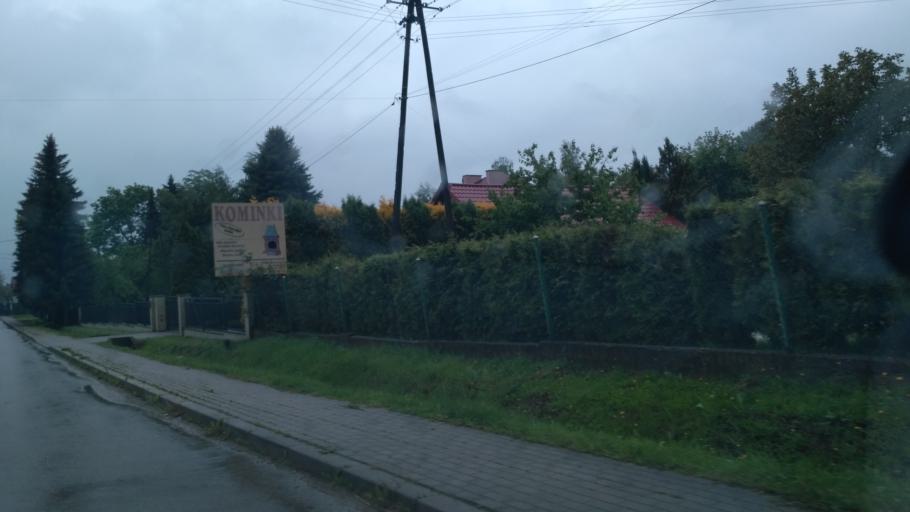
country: PL
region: Subcarpathian Voivodeship
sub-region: Powiat jasielski
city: Tarnowiec
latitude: 49.7659
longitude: 21.5409
